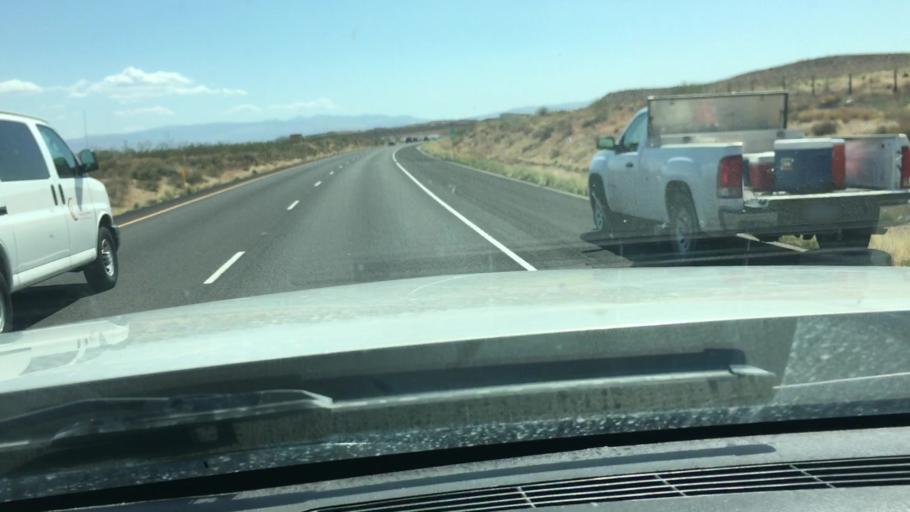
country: US
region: Utah
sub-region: Washington County
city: Washington
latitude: 37.1818
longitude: -113.4165
